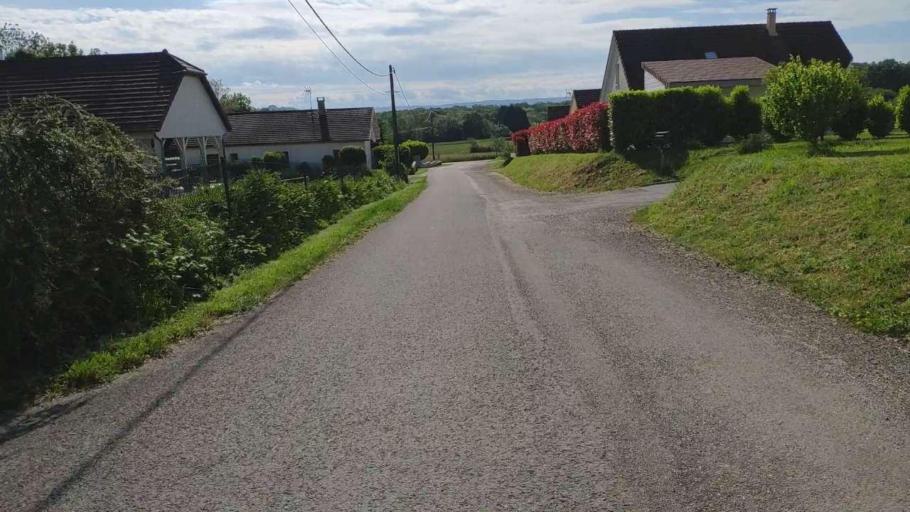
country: FR
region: Franche-Comte
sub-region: Departement du Jura
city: Bletterans
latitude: 46.7160
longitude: 5.4706
